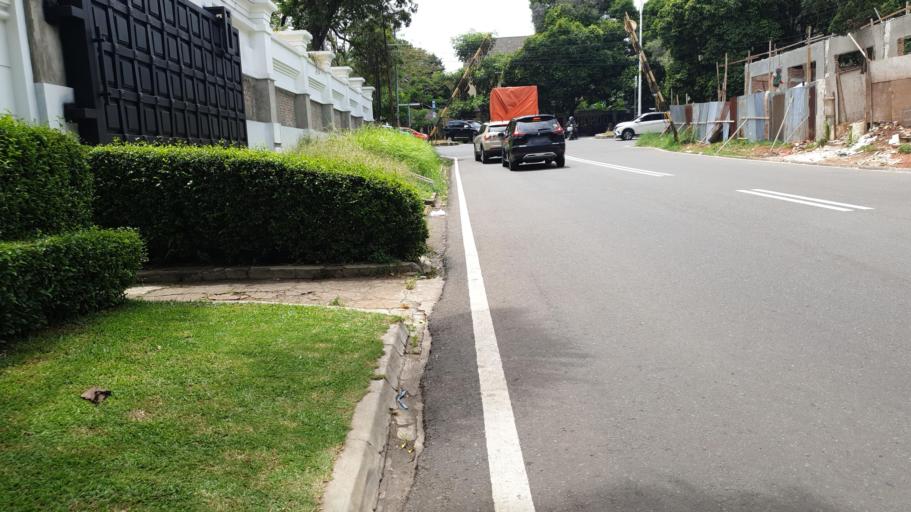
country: ID
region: Banten
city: South Tangerang
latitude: -6.2809
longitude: 106.7842
